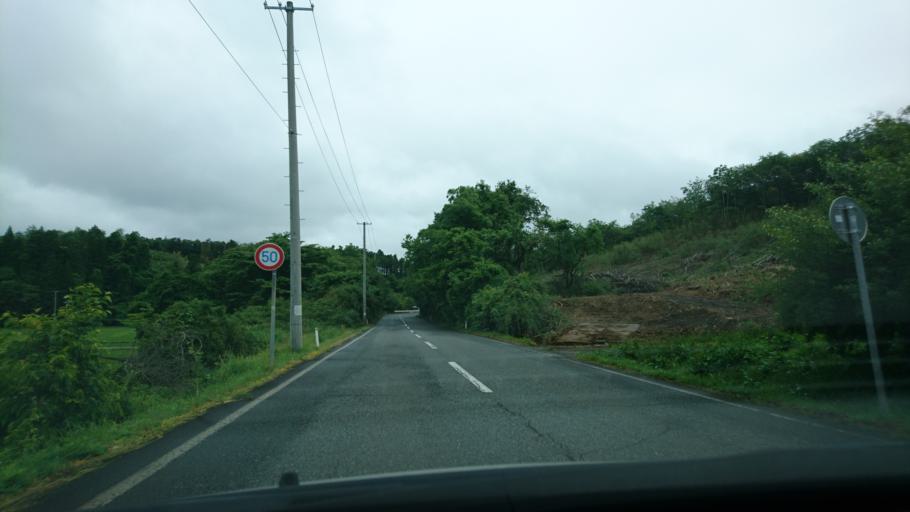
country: JP
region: Iwate
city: Ichinoseki
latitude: 38.8947
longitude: 141.1526
